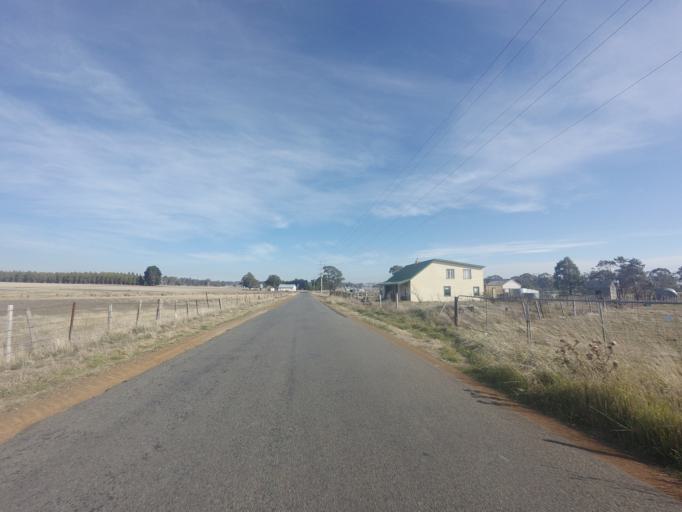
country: AU
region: Tasmania
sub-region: Sorell
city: Sorell
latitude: -42.4402
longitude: 147.4720
